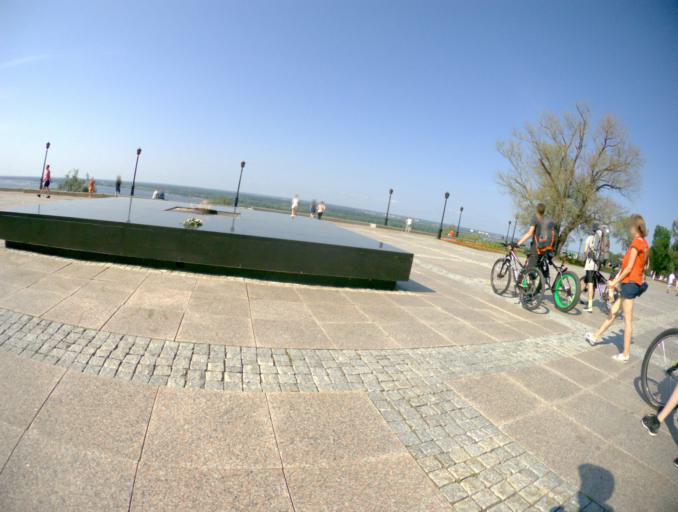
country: RU
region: Nizjnij Novgorod
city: Nizhniy Novgorod
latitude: 56.3287
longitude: 44.0012
